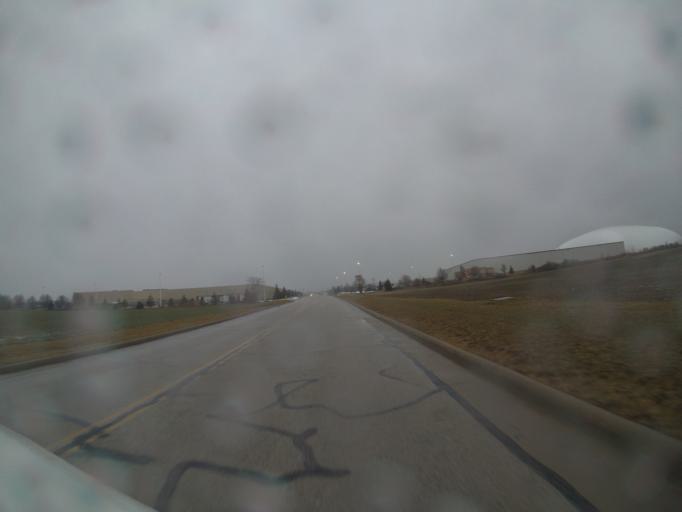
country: US
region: Ohio
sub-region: Wood County
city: Perrysburg
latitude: 41.5477
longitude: -83.5860
